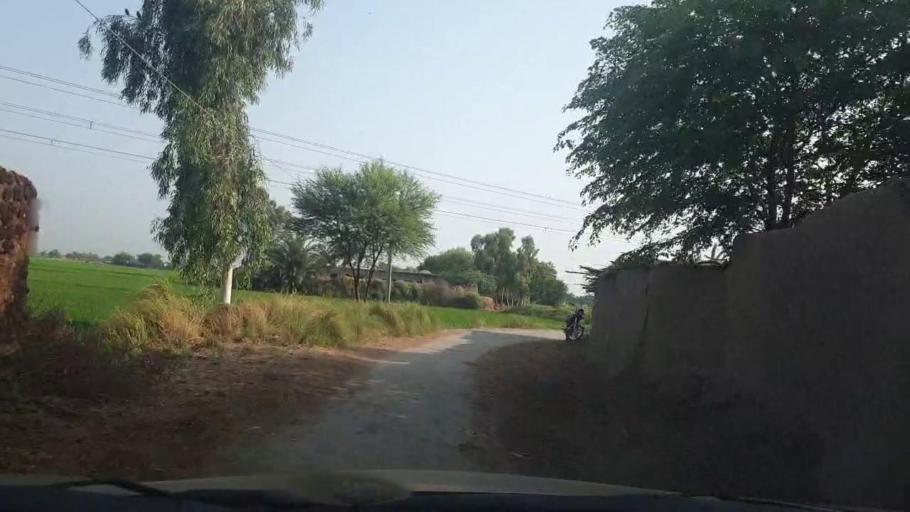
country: PK
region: Sindh
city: Larkana
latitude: 27.5912
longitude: 68.1605
